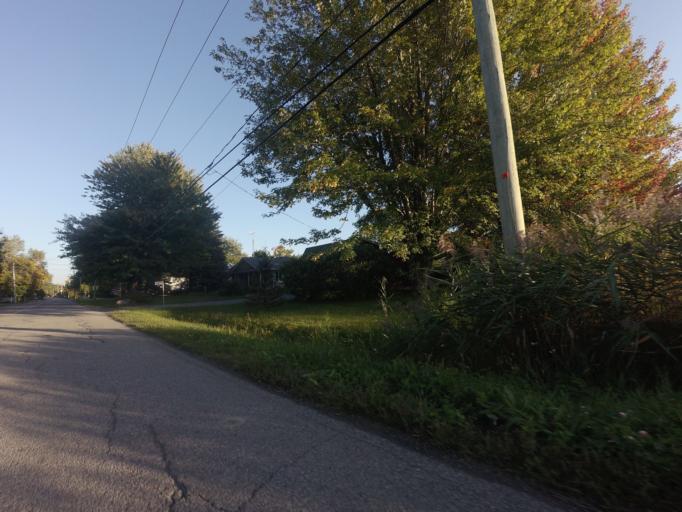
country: CA
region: Quebec
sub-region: Monteregie
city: Rigaud
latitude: 45.4803
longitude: -74.2460
